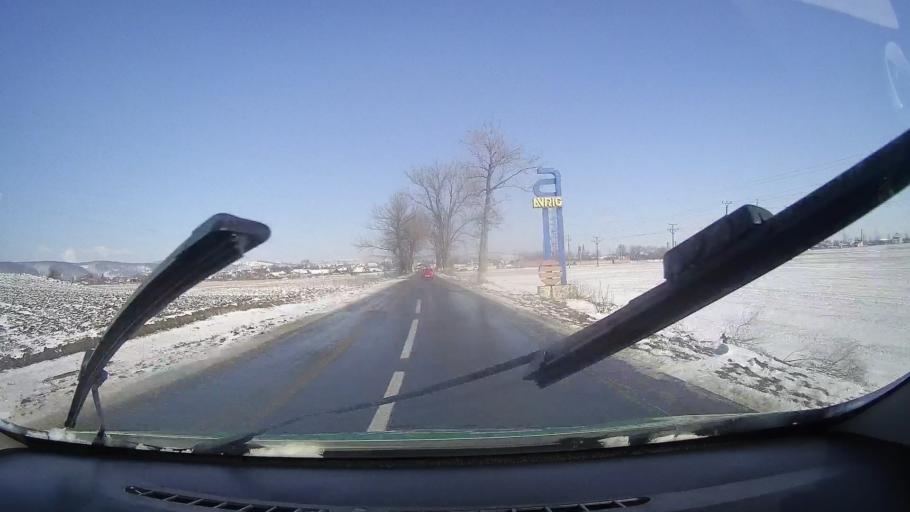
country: RO
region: Sibiu
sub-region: Comuna Avrig
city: Avrig
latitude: 45.7162
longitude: 24.3729
